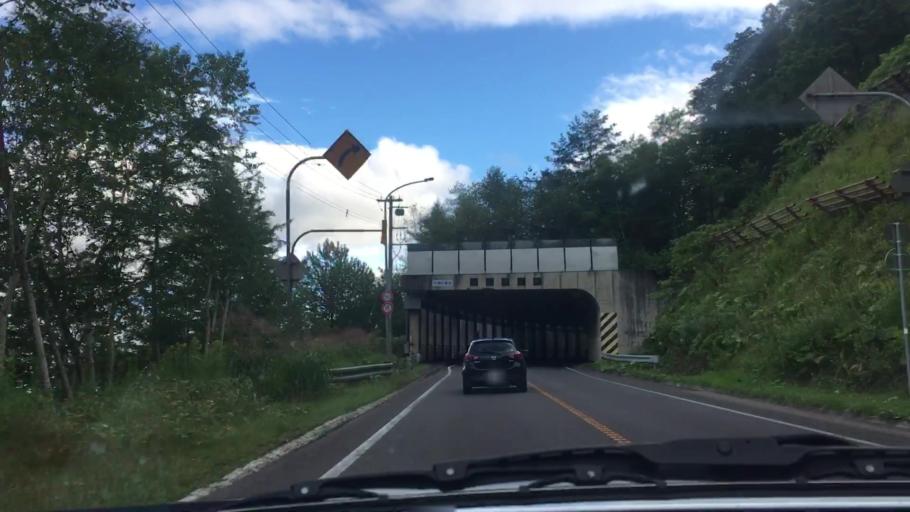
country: JP
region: Hokkaido
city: Shimo-furano
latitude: 43.1448
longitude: 142.7708
